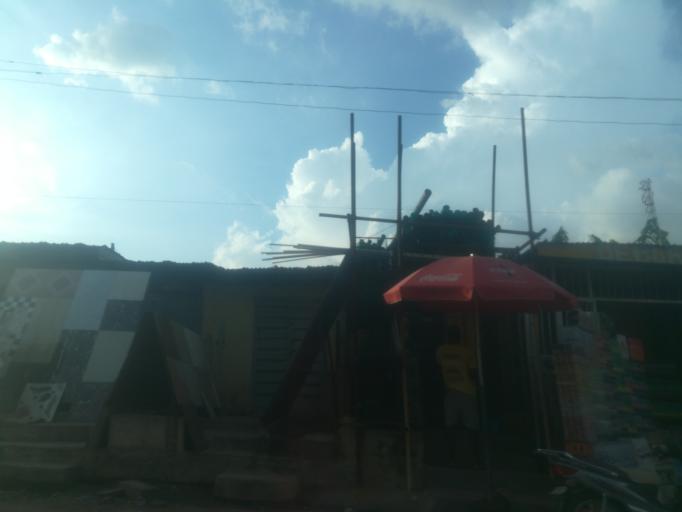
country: NG
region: Oyo
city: Ibadan
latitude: 7.3862
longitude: 3.8745
